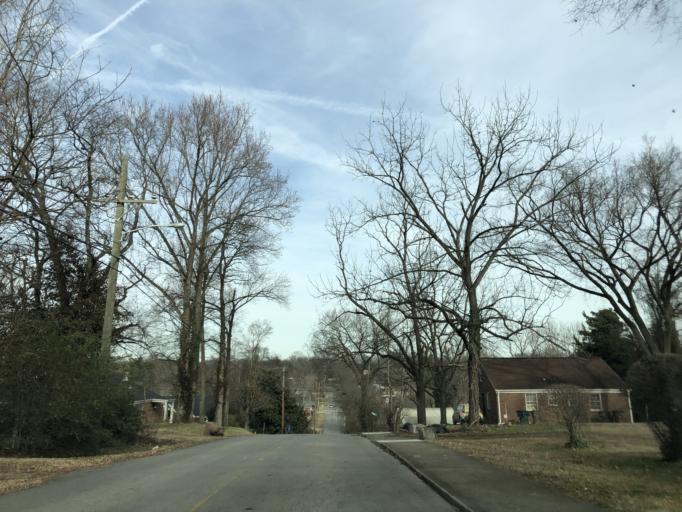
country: US
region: Tennessee
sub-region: Davidson County
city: Nashville
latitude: 36.2134
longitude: -86.7215
